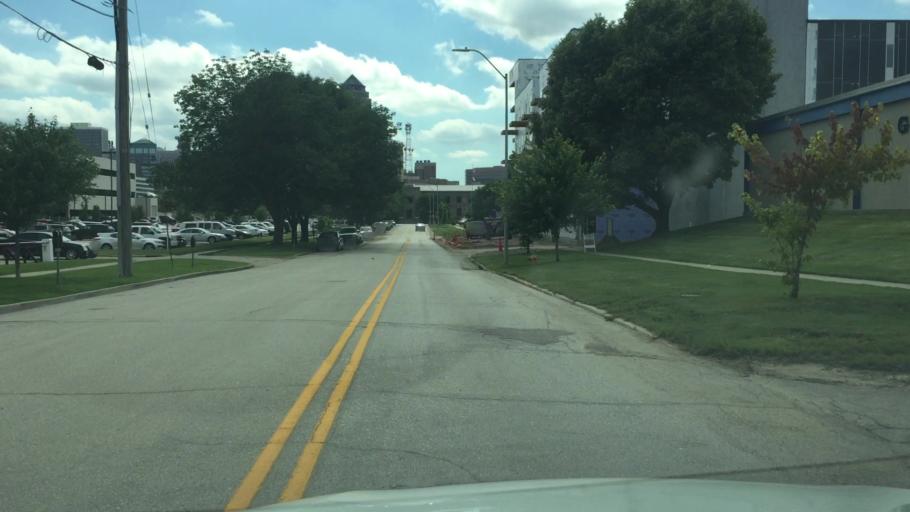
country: US
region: Iowa
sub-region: Polk County
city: Des Moines
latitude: 41.5913
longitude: -93.6138
